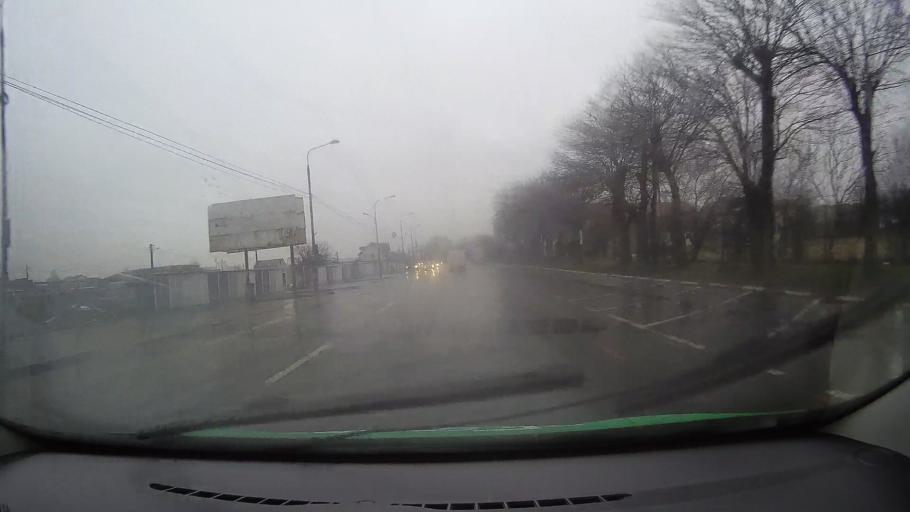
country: RO
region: Sibiu
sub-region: Municipiul Sibiu
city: Sibiu
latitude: 45.8170
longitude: 24.1496
